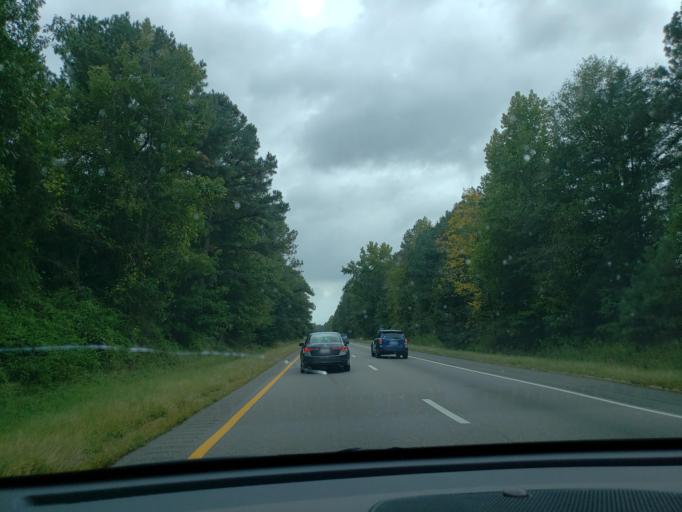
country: US
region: Virginia
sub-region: Mecklenburg County
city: Bracey
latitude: 36.5619
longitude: -78.1798
